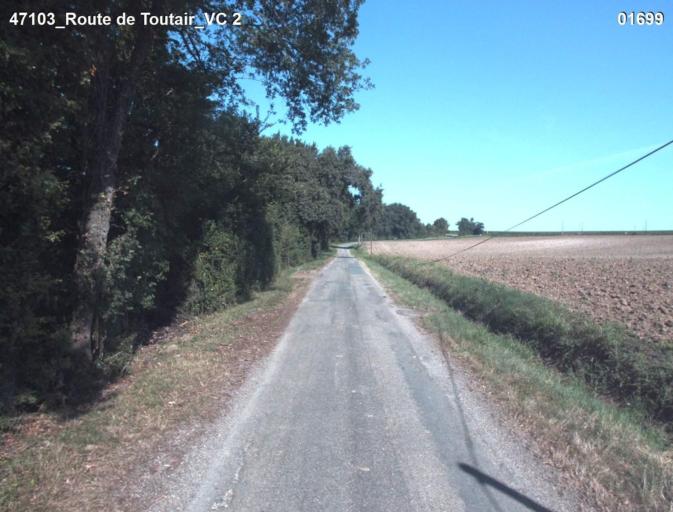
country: FR
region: Aquitaine
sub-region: Departement du Lot-et-Garonne
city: Nerac
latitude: 44.0735
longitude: 0.3317
